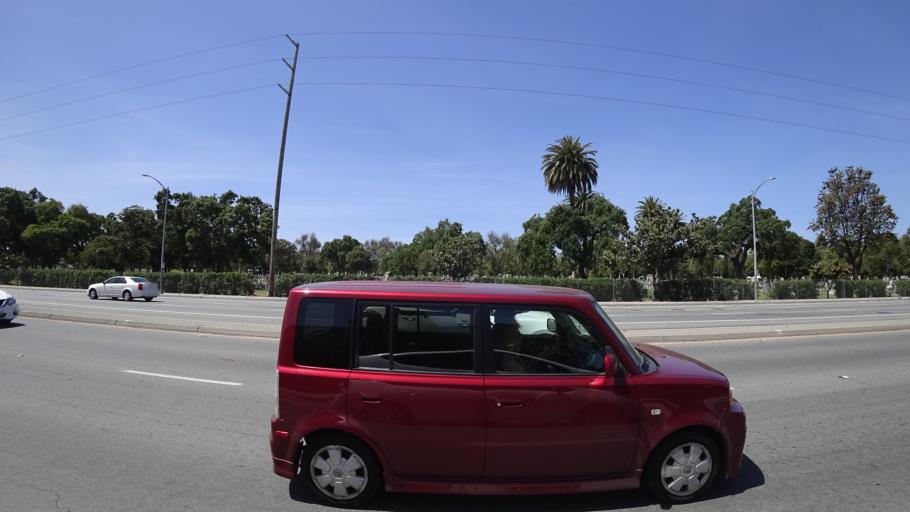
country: US
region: California
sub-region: Santa Clara County
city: Seven Trees
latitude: 37.3012
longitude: -121.8587
